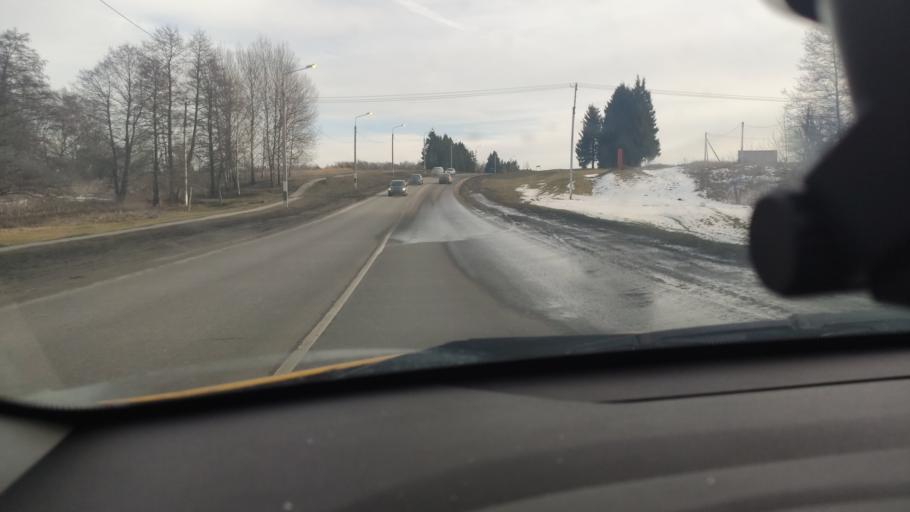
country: RU
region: Moskovskaya
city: Dubrovitsy
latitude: 55.4141
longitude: 37.4100
